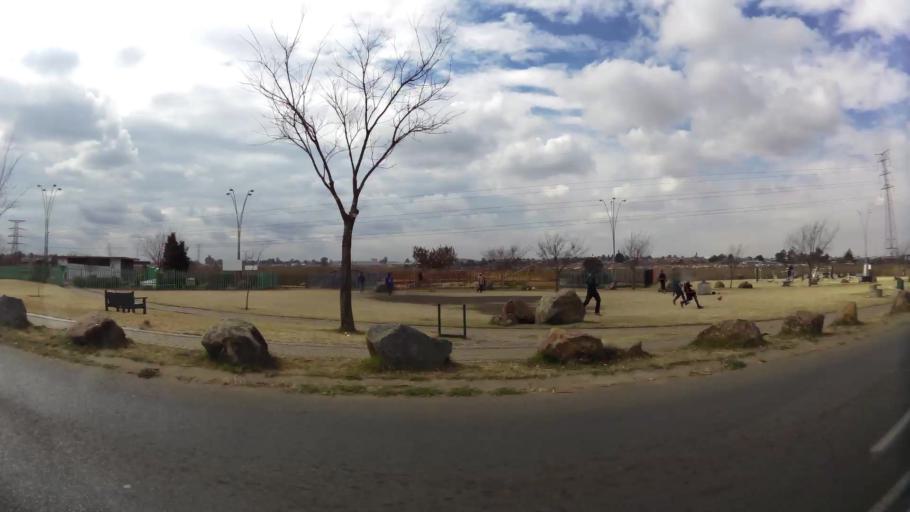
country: ZA
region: Gauteng
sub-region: City of Johannesburg Metropolitan Municipality
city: Soweto
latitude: -26.2685
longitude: 27.8809
